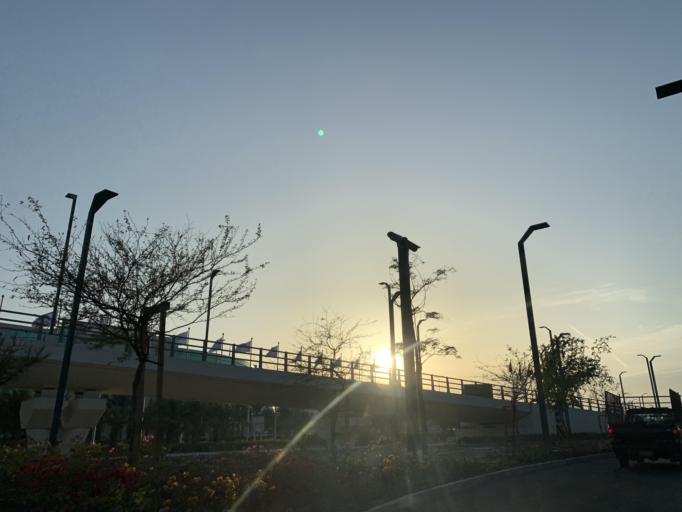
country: BH
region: Muharraq
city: Al Muharraq
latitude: 26.2667
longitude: 50.6278
